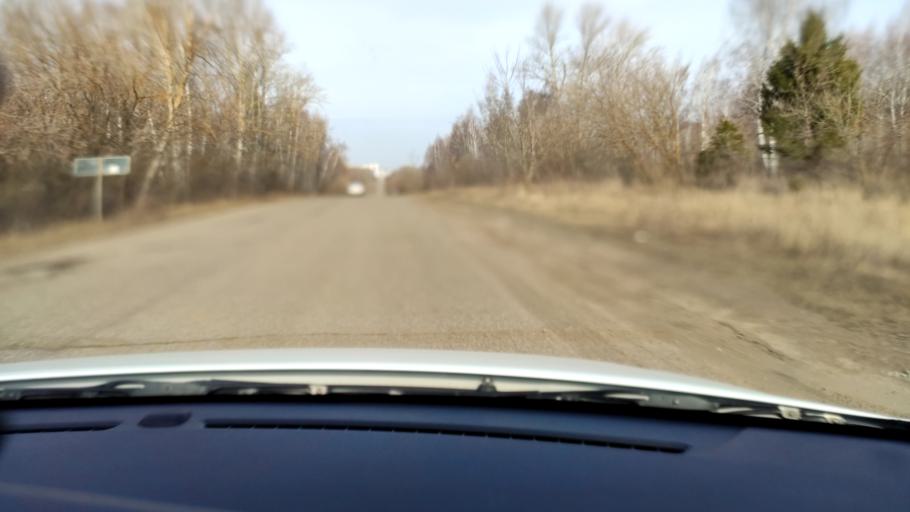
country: RU
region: Tatarstan
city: Stolbishchi
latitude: 55.7176
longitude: 49.2180
